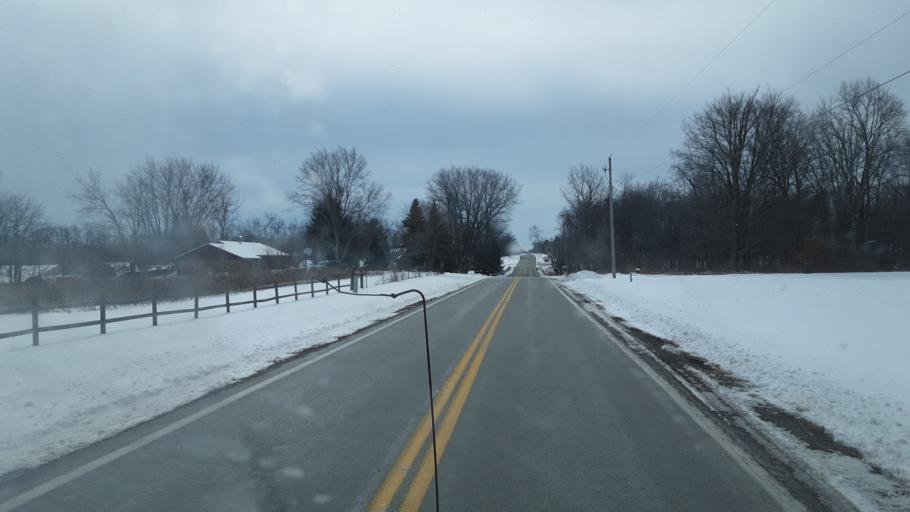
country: US
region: Ohio
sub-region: Madison County
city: Choctaw Lake
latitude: 39.9799
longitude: -83.4996
